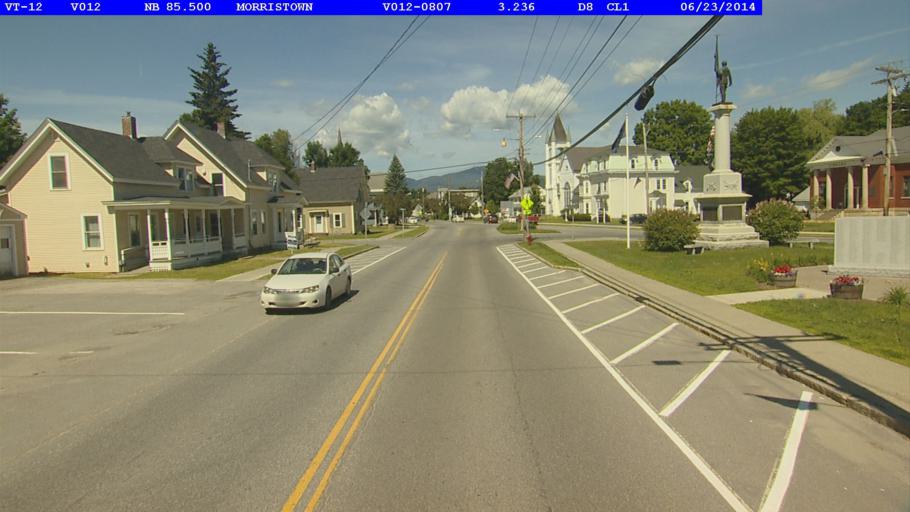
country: US
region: Vermont
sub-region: Lamoille County
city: Morrisville
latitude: 44.5617
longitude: -72.5950
